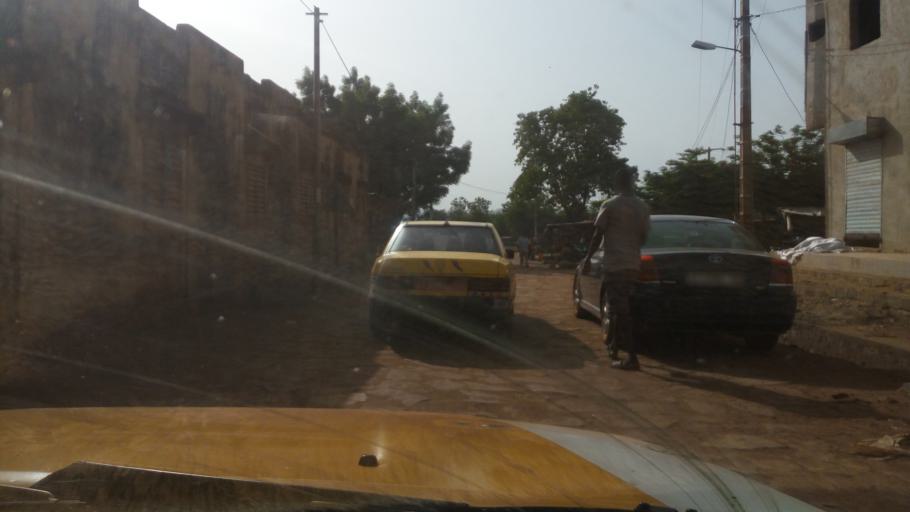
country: ML
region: Bamako
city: Bamako
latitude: 12.6081
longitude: -8.0064
